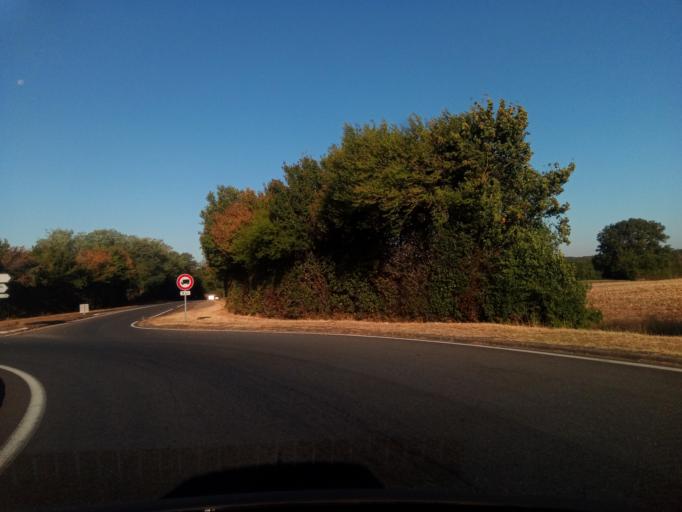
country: FR
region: Poitou-Charentes
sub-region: Departement de la Vienne
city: Lussac-les-Chateaux
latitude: 46.4006
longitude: 0.7411
